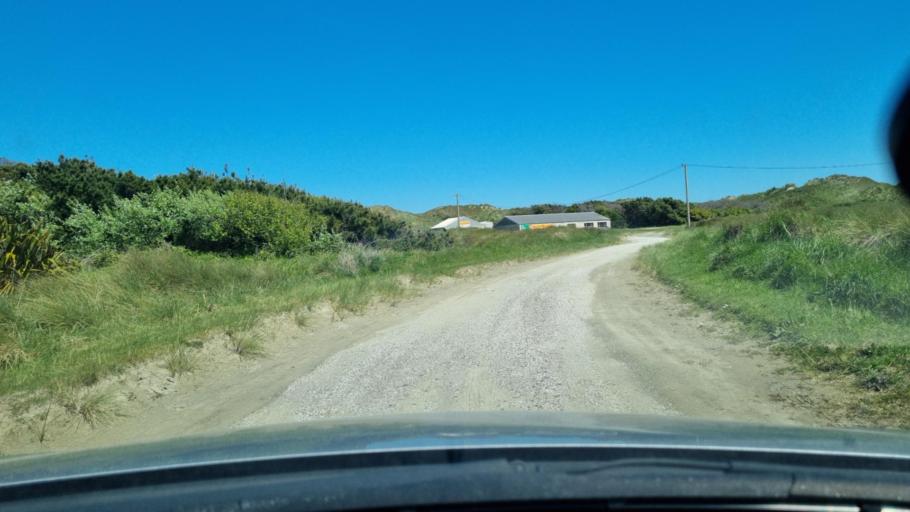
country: NZ
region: Southland
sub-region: Invercargill City
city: Invercargill
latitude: -46.4387
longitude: 168.2362
